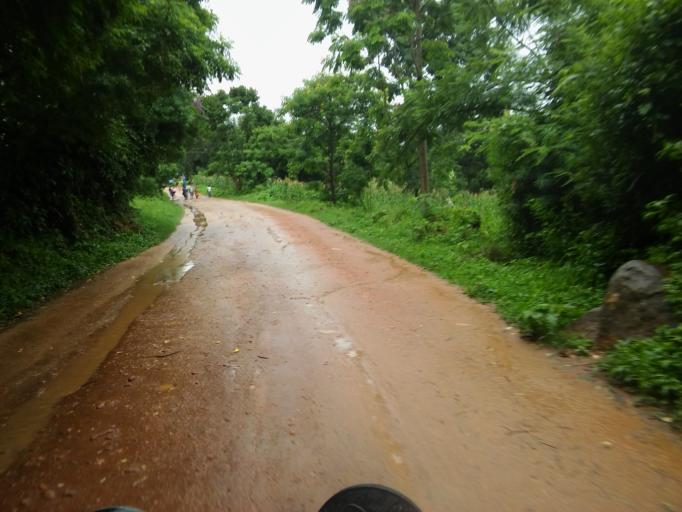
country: UG
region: Eastern Region
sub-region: Mbale District
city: Mbale
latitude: 0.9860
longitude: 34.2151
